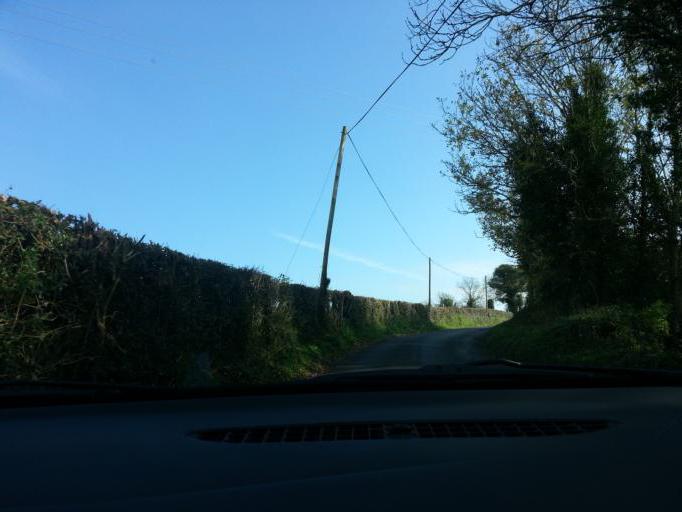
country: GB
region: Northern Ireland
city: Lisnaskea
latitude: 54.2471
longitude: -7.4196
